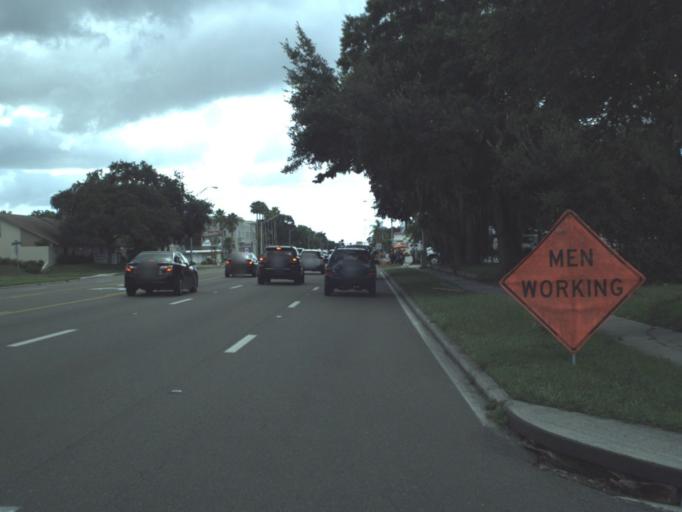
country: US
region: Florida
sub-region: Sarasota County
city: Southgate
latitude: 27.3131
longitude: -82.5299
